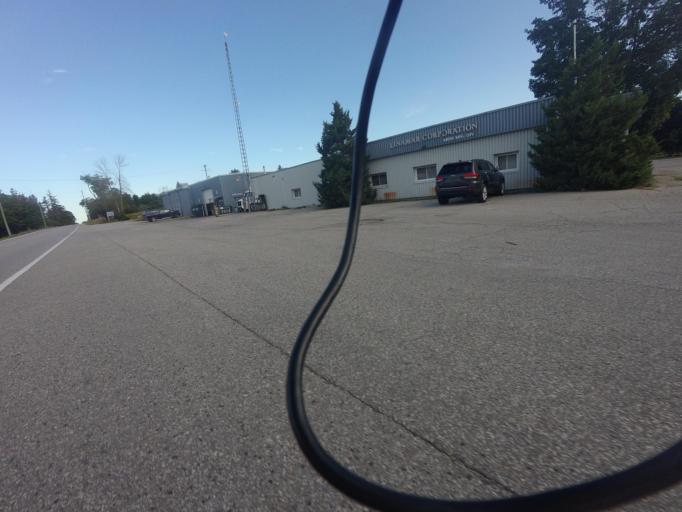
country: CA
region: Ontario
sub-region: Wellington County
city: Guelph
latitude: 43.5788
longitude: -80.3340
